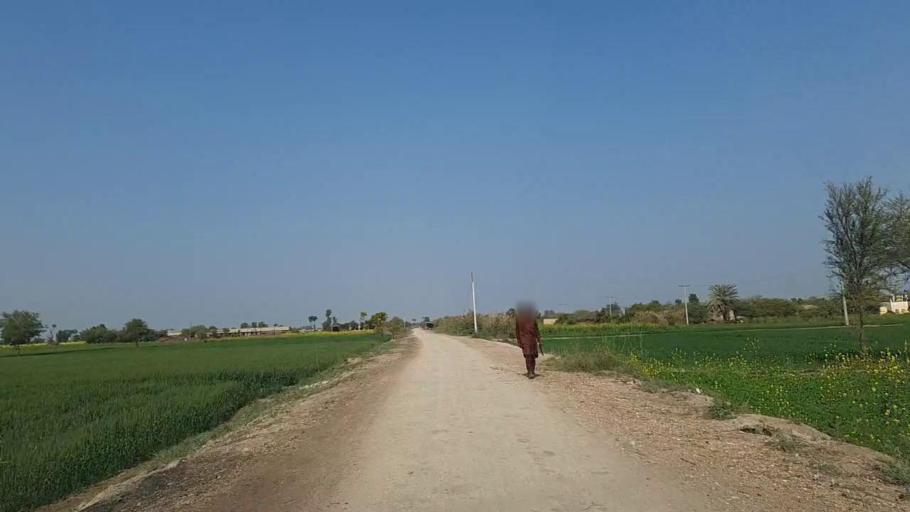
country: PK
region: Sindh
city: Nawabshah
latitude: 26.2794
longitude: 68.5136
